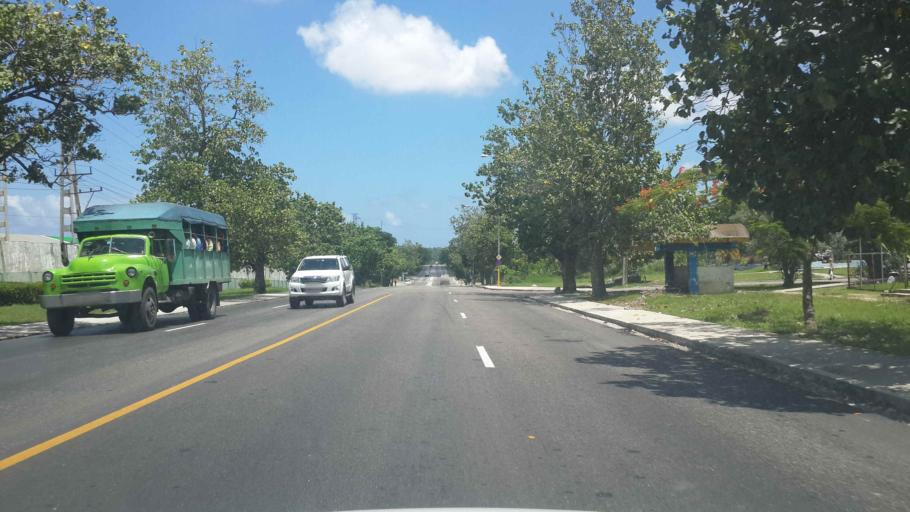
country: CU
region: La Habana
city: Guanabacoa
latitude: 23.1350
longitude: -82.3096
